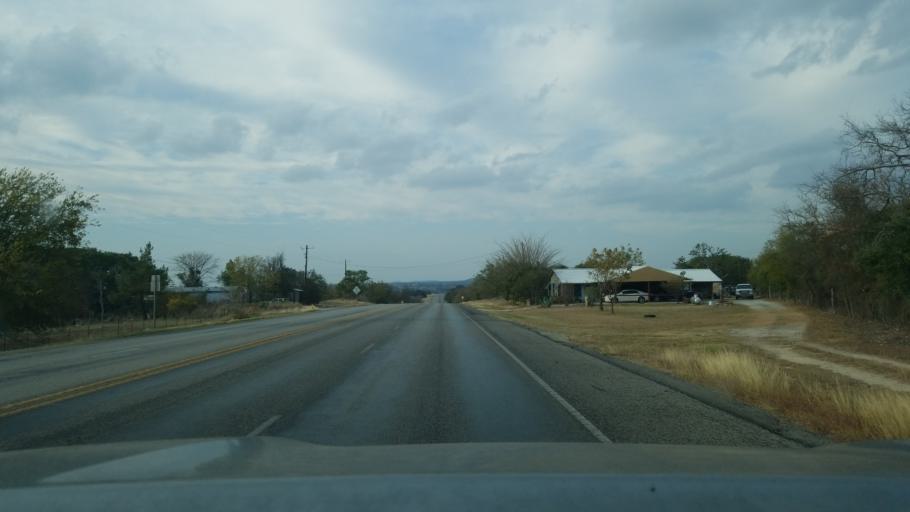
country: US
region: Texas
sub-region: Mills County
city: Goldthwaite
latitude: 31.4896
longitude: -98.5742
